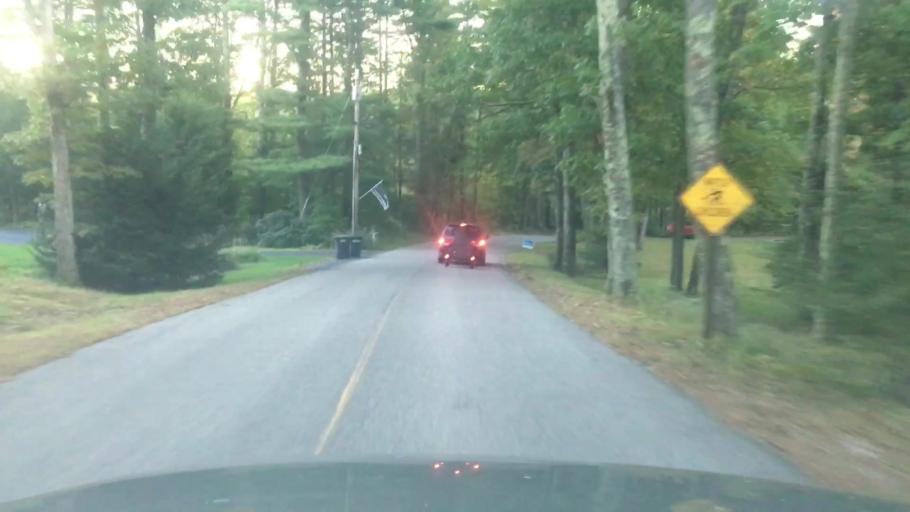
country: US
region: Massachusetts
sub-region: Worcester County
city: Southbridge
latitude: 42.1209
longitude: -72.0289
